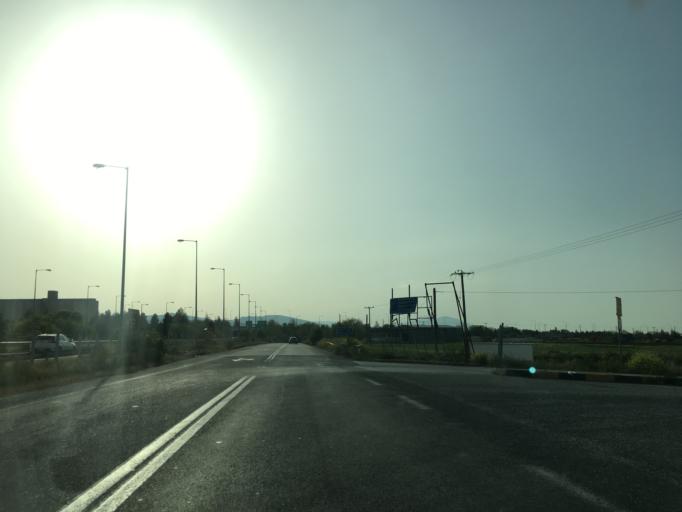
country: GR
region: Thessaly
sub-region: Nomos Magnisias
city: Velestino
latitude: 39.3887
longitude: 22.7706
